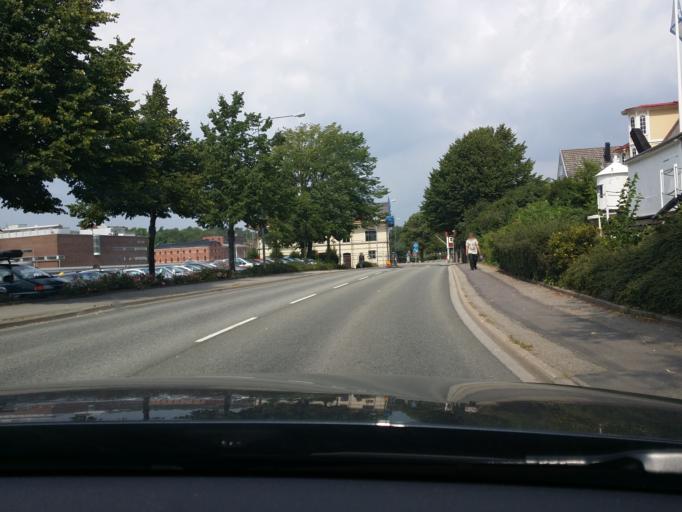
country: SE
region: Blekinge
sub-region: Karlshamns Kommun
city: Karlshamn
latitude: 56.1655
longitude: 14.8651
